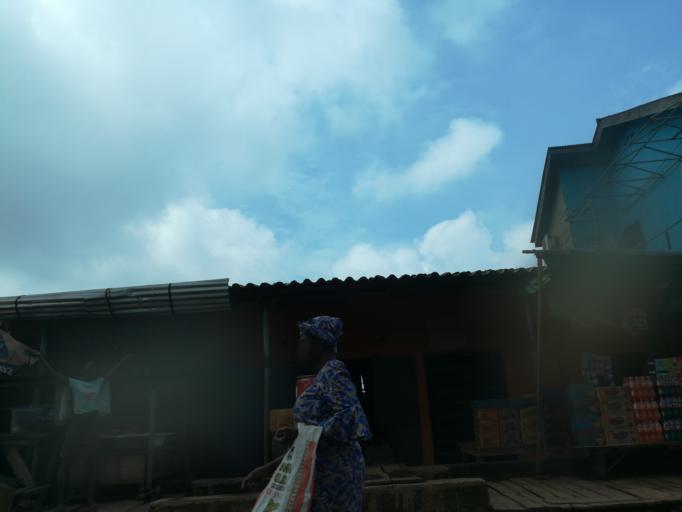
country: NG
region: Lagos
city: Ikorodu
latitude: 6.6630
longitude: 3.5188
